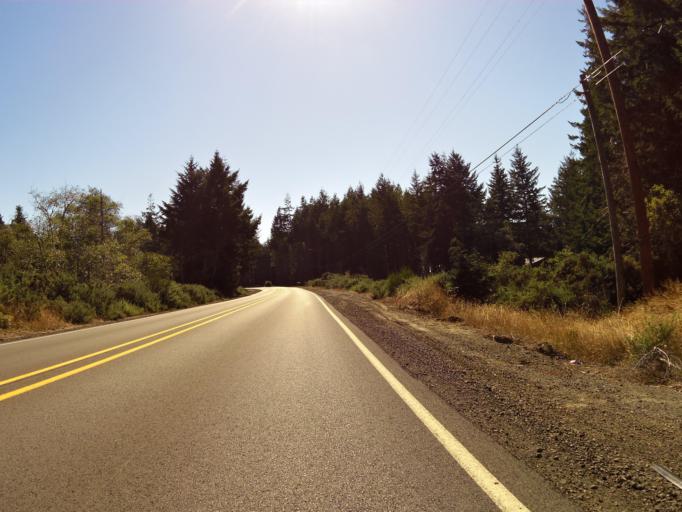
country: US
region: Oregon
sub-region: Coos County
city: Bandon
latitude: 43.1942
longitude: -124.3667
